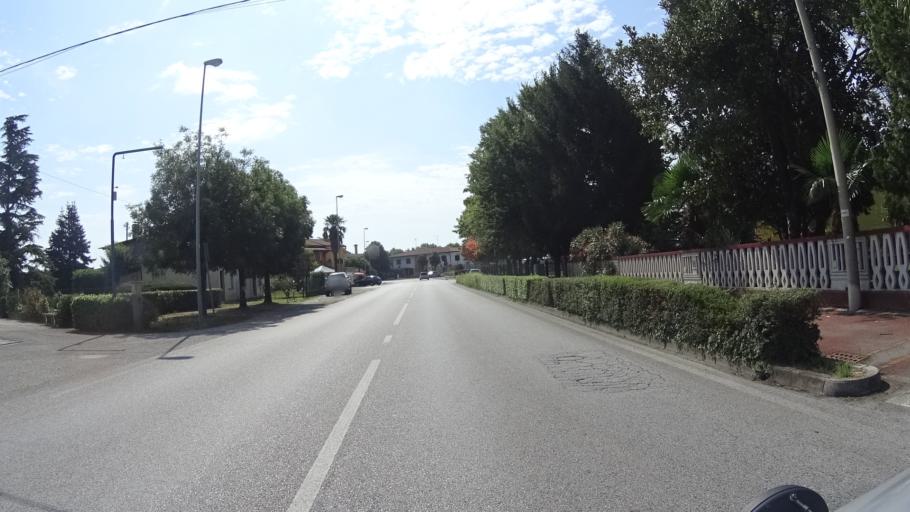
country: IT
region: Friuli Venezia Giulia
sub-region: Provincia di Udine
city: Latisana
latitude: 45.7725
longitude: 13.0178
